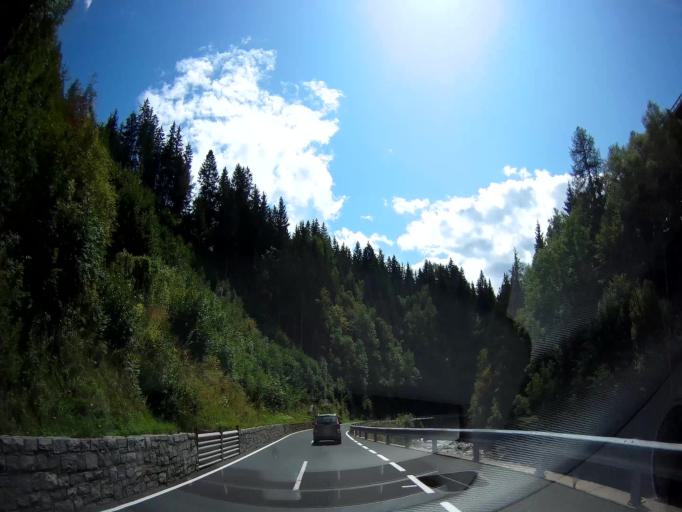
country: AT
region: Carinthia
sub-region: Politischer Bezirk Spittal an der Drau
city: Trebesing
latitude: 46.8613
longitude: 13.5042
